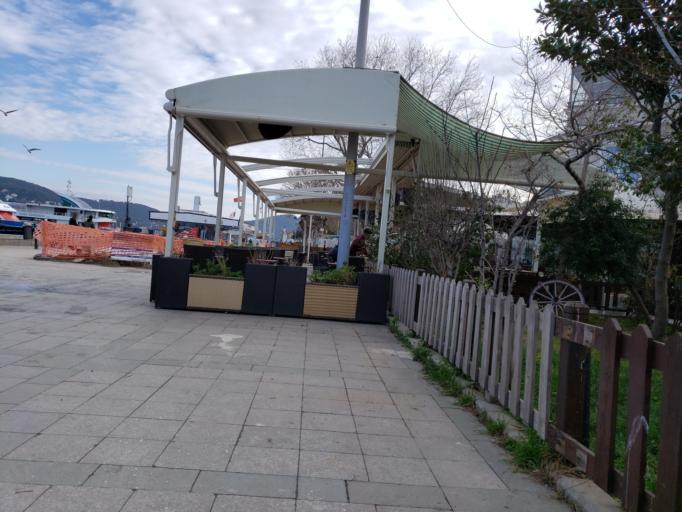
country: TR
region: Istanbul
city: Adalan
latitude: 40.8787
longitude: 29.1001
